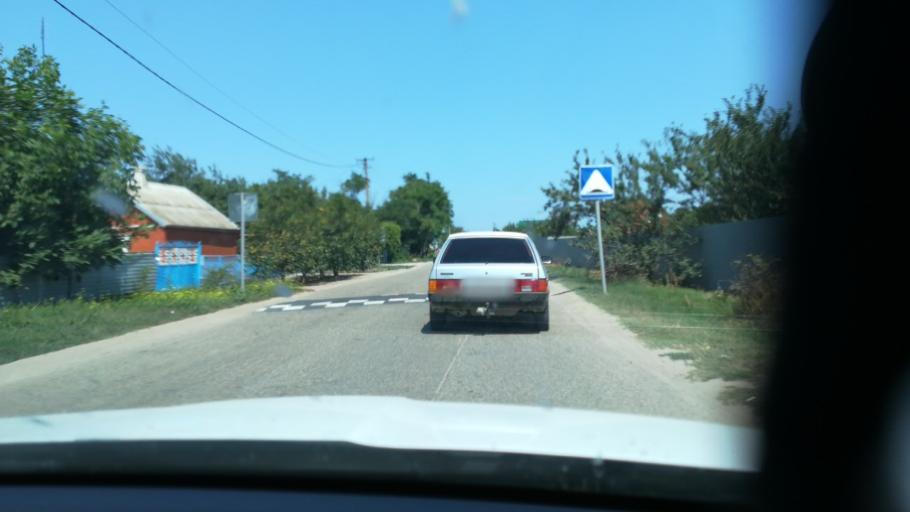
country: RU
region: Krasnodarskiy
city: Starotitarovskaya
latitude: 45.2063
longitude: 37.1467
